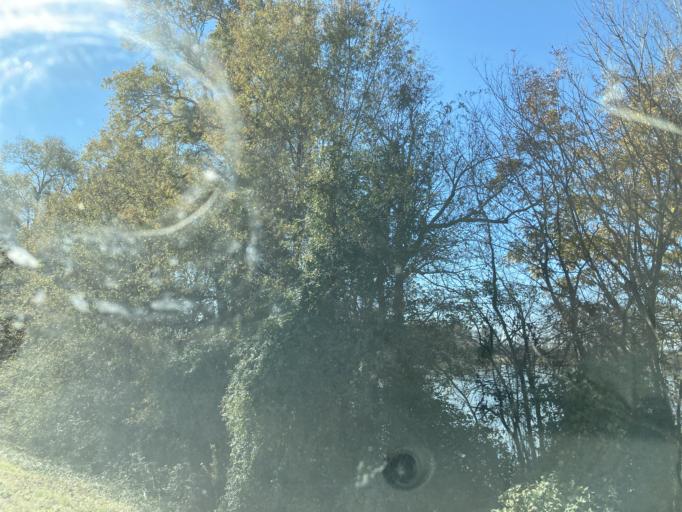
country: US
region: Mississippi
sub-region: Yazoo County
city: Yazoo City
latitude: 32.9253
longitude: -90.4940
